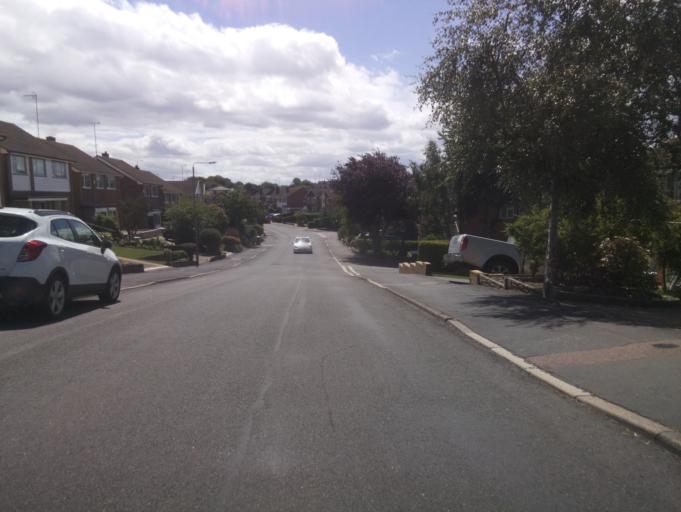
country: GB
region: England
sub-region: Nottinghamshire
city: Cotgrave
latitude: 52.8765
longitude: -1.0833
